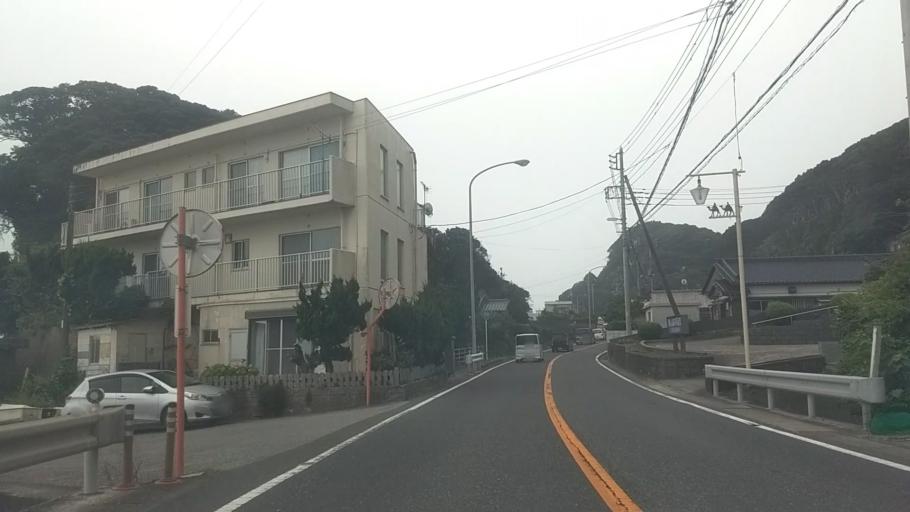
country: JP
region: Chiba
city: Katsuura
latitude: 35.1783
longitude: 140.3476
